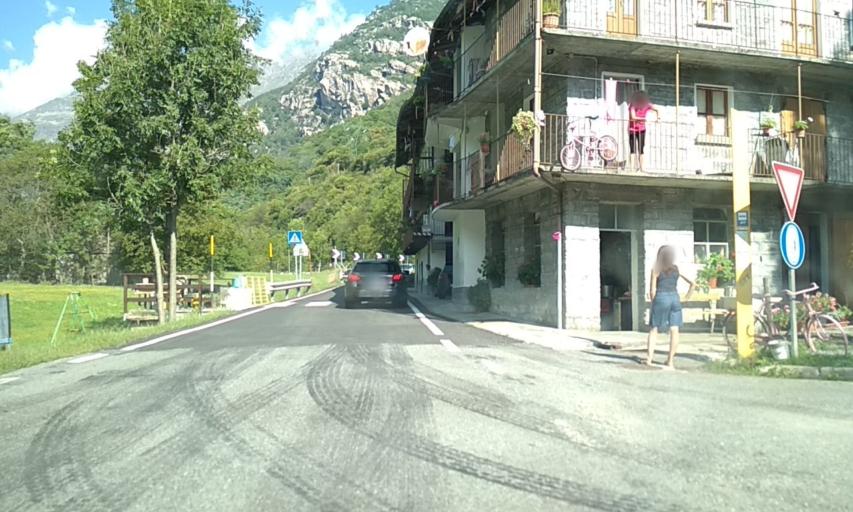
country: IT
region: Piedmont
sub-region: Provincia di Torino
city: Noasca
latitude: 45.4393
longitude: 7.3459
